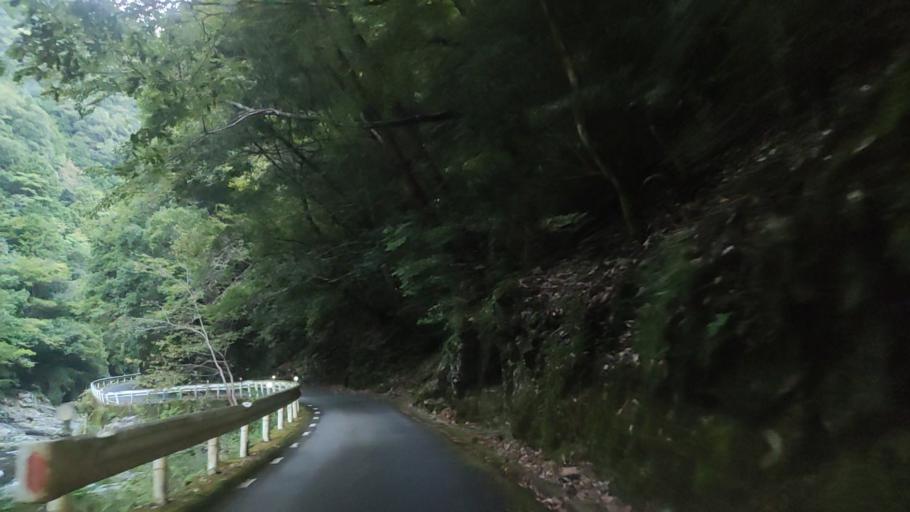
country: JP
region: Wakayama
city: Koya
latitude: 34.2538
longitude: 135.6514
